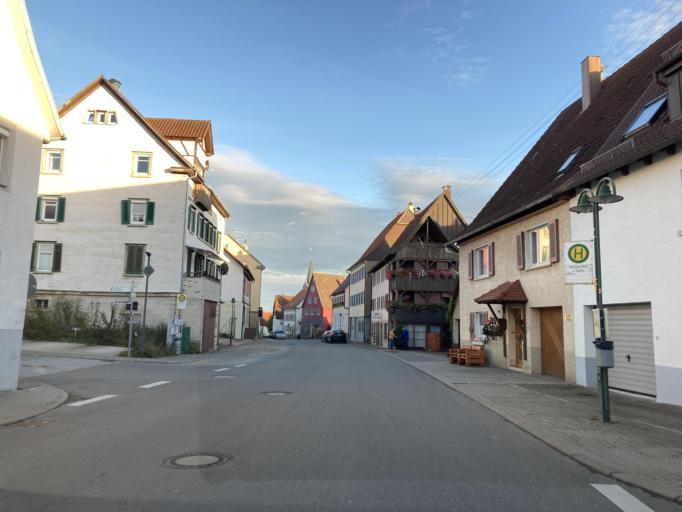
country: DE
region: Baden-Wuerttemberg
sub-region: Regierungsbezirk Stuttgart
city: Motzingen
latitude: 48.5058
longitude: 8.7726
